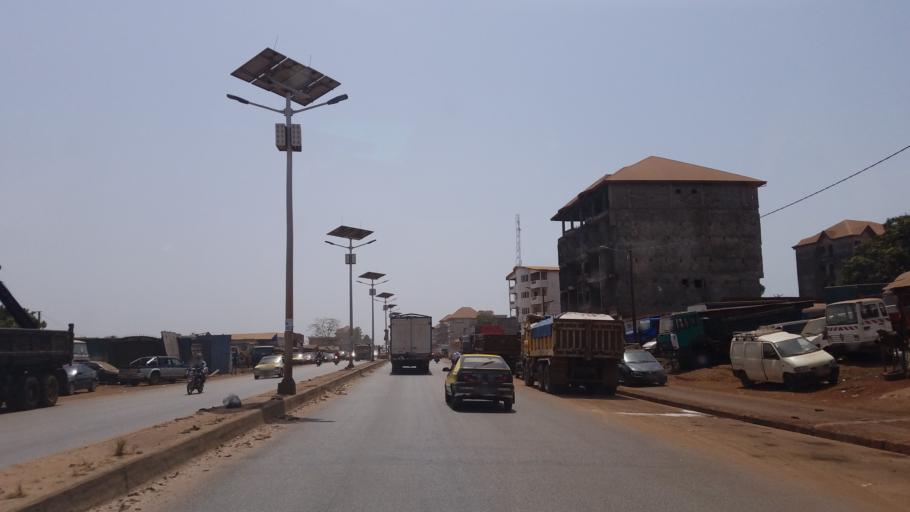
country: GN
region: Kindia
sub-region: Prefecture de Dubreka
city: Dubreka
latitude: 9.6555
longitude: -13.5725
